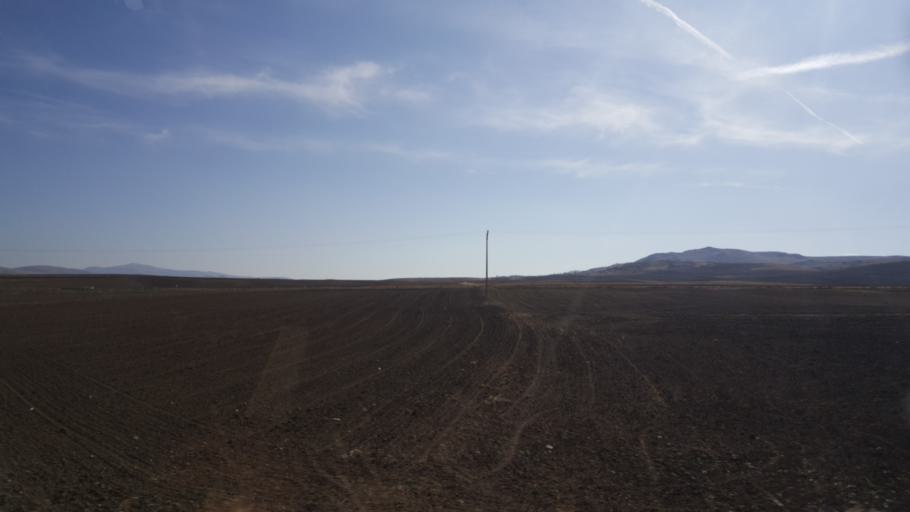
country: TR
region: Ankara
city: Yenice
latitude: 39.3751
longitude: 32.7359
